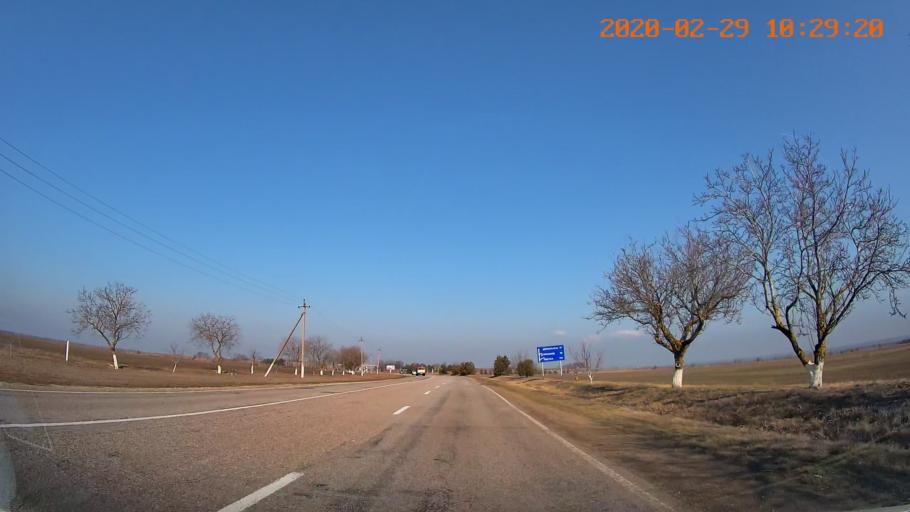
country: MD
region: Telenesti
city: Tiraspolul Nou
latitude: 46.9224
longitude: 29.5863
